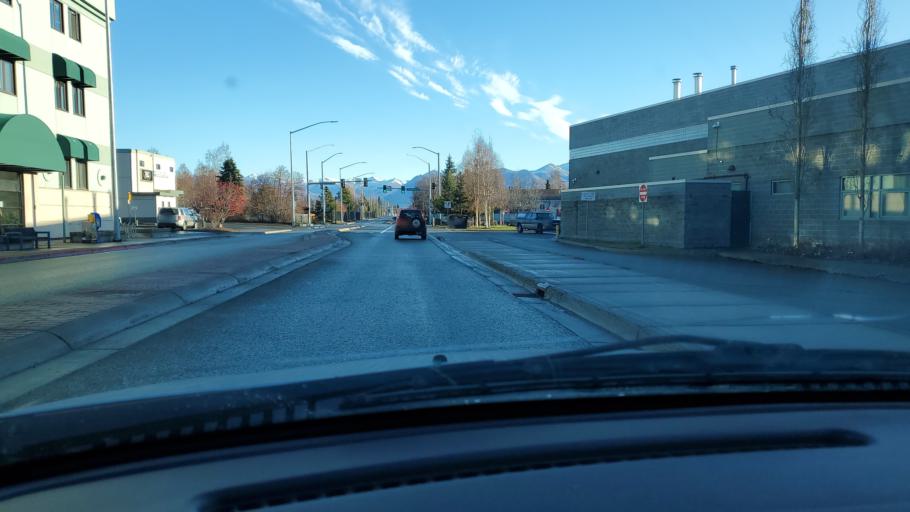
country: US
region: Alaska
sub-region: Anchorage Municipality
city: Anchorage
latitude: 61.2136
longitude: -149.8813
